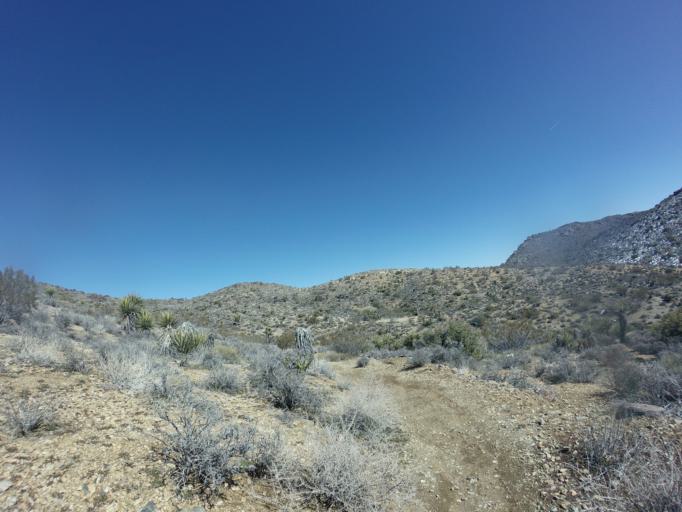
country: US
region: California
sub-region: San Bernardino County
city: Twentynine Palms
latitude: 33.9302
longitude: -116.1326
